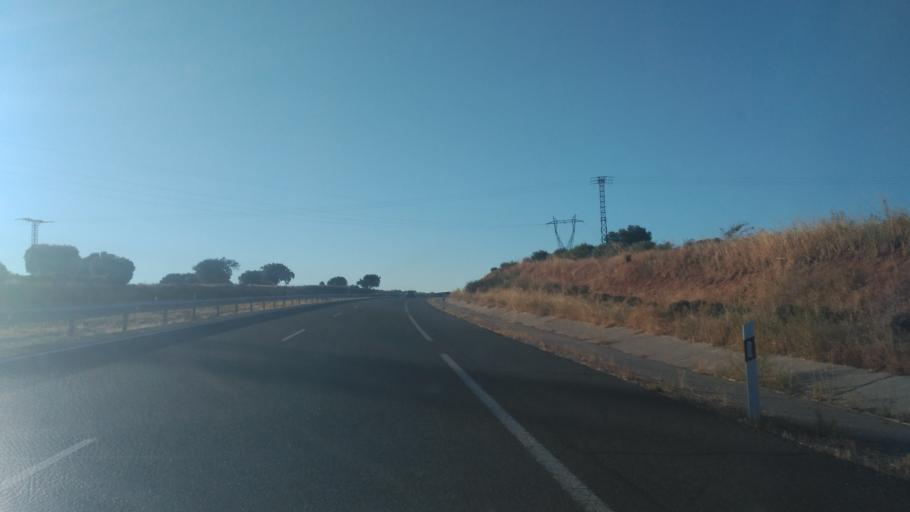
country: ES
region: Castille and Leon
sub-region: Provincia de Salamanca
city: Belena
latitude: 40.7215
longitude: -5.6297
